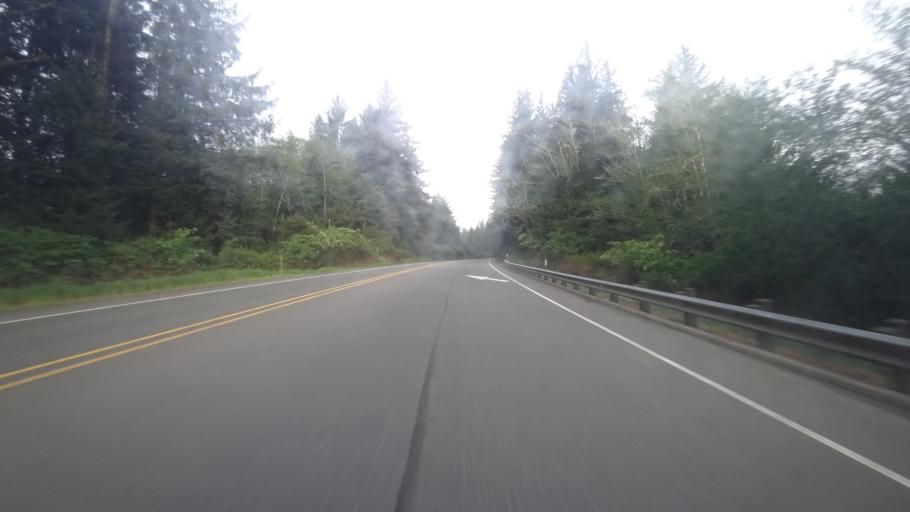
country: US
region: Oregon
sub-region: Coos County
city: Barview
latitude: 43.2545
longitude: -124.2784
